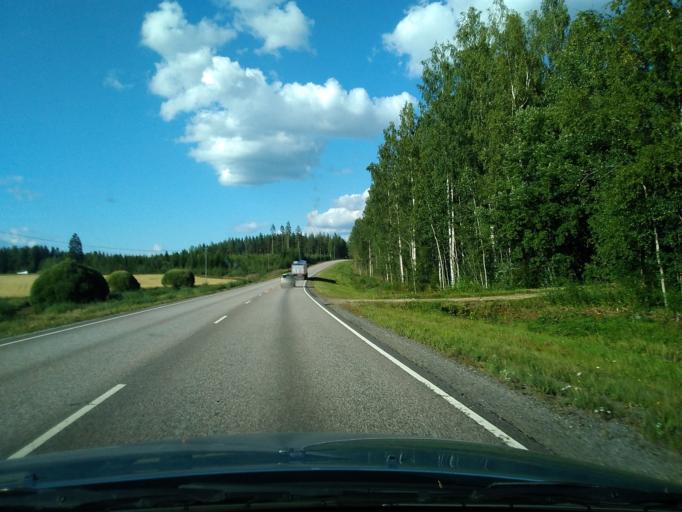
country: FI
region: Central Finland
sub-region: Keuruu
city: Keuruu
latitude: 62.1308
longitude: 24.7364
